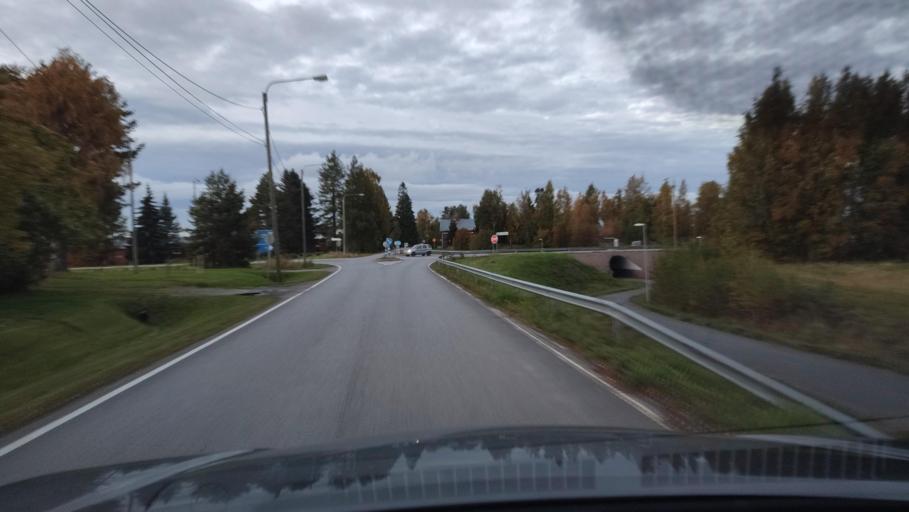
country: FI
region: Ostrobothnia
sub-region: Sydosterbotten
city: Kristinestad
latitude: 62.2599
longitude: 21.5081
